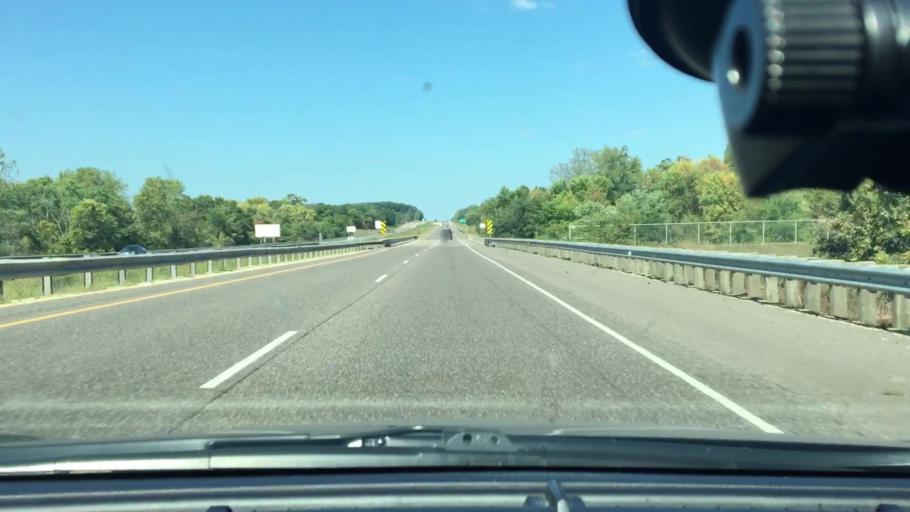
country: US
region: Wisconsin
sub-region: Eau Claire County
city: Eau Claire
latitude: 44.7849
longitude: -91.5438
